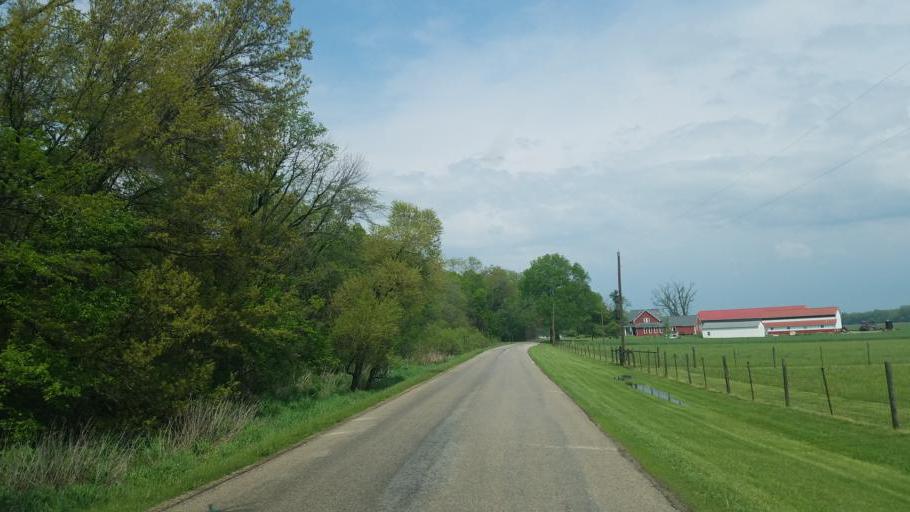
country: US
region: Ohio
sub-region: Licking County
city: Hebron
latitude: 39.9469
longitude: -82.5096
